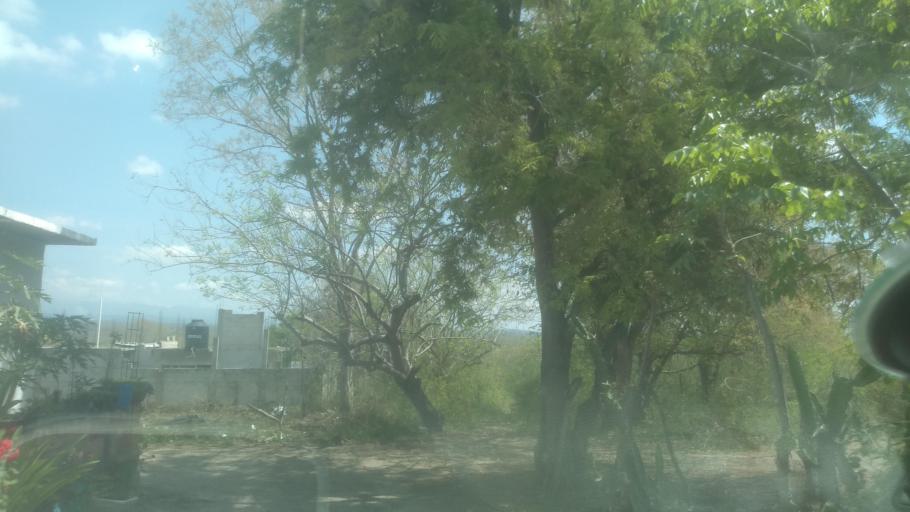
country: MX
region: Veracruz
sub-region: Emiliano Zapata
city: Plan del Rio
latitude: 19.3945
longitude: -96.6348
